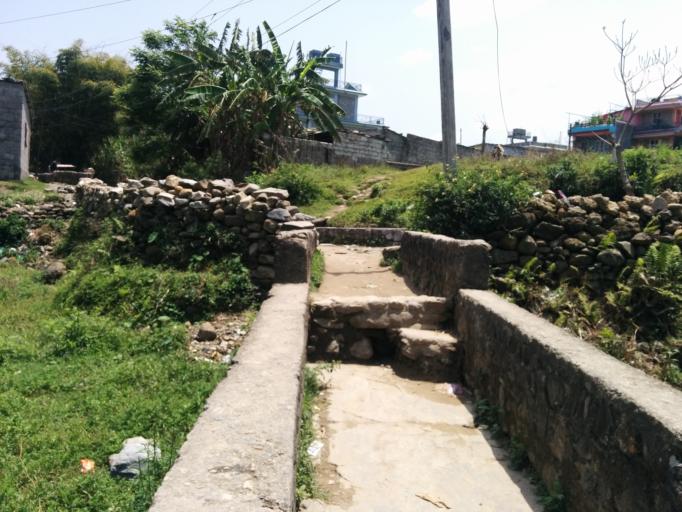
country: NP
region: Western Region
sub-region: Gandaki Zone
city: Pokhara
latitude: 28.1938
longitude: 83.9678
